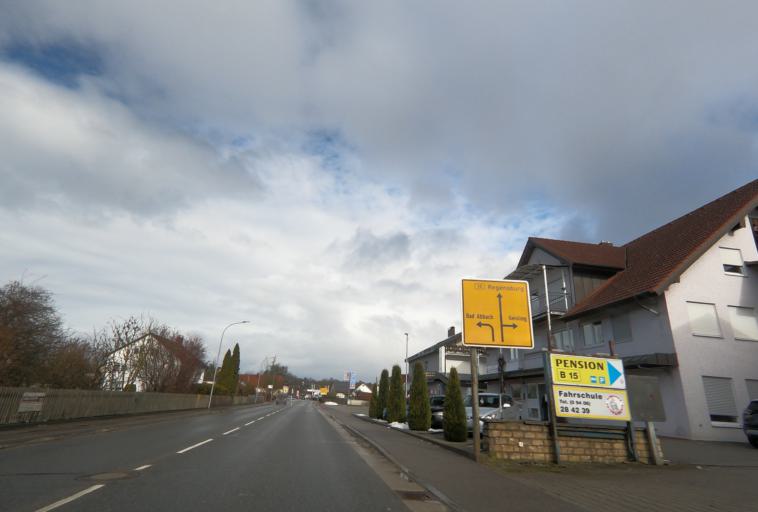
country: DE
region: Bavaria
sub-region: Upper Palatinate
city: Kofering
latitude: 48.9380
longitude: 12.2019
